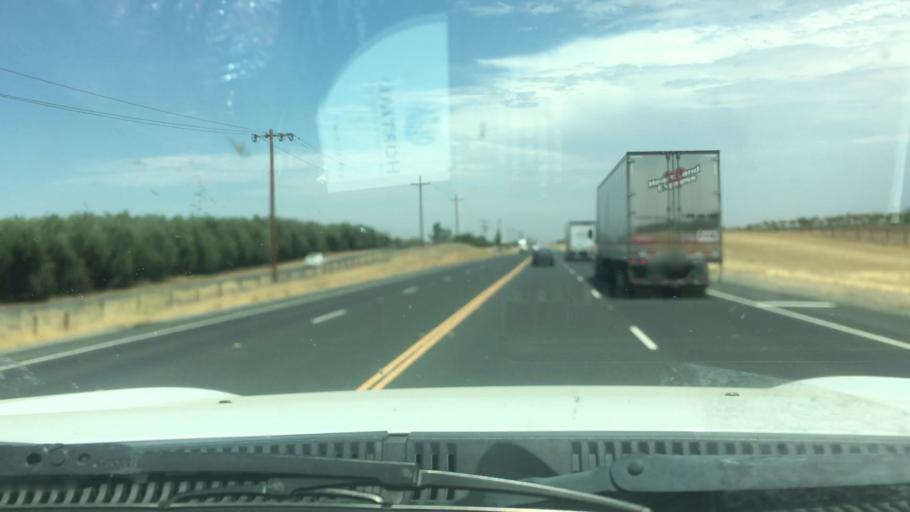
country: US
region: California
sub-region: Tulare County
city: Terra Bella
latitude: 35.9210
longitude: -119.0535
